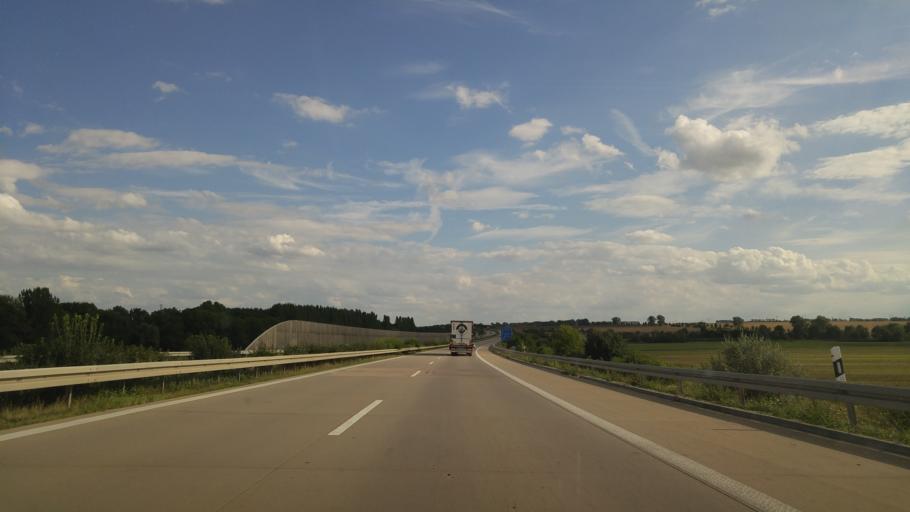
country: DE
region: Saxony-Anhalt
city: Bad Lauchstadt
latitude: 51.3790
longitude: 11.9120
